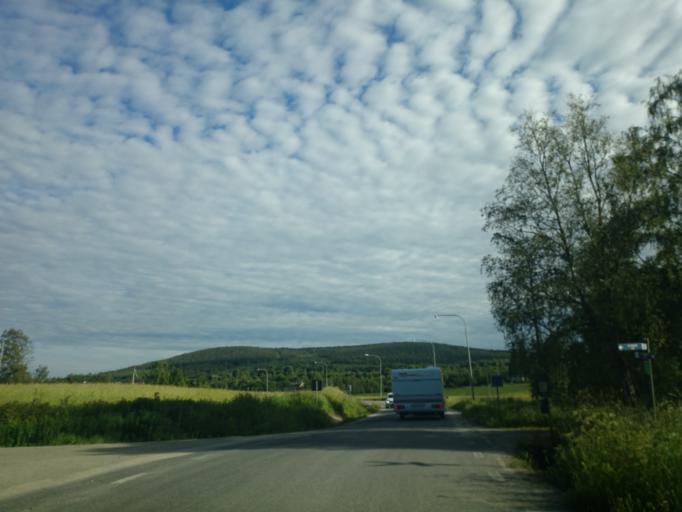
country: SE
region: Vaesternorrland
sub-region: Haernoesands Kommun
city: Haernoesand
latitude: 62.6189
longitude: 17.8787
